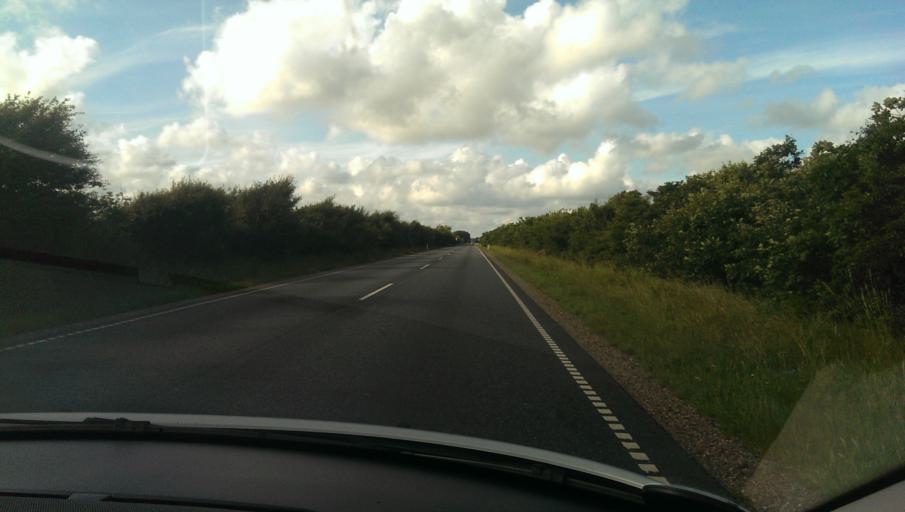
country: DK
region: Central Jutland
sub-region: Ringkobing-Skjern Kommune
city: Ringkobing
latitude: 56.1663
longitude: 8.2867
